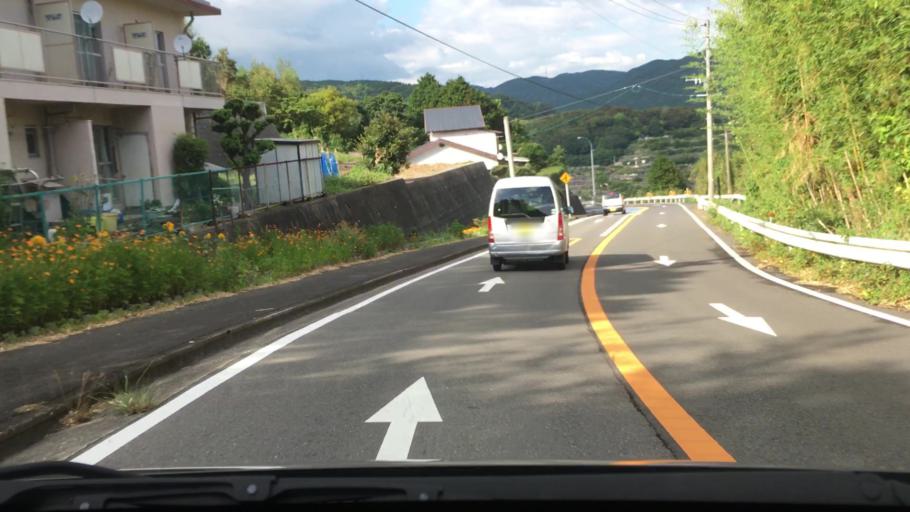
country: JP
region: Nagasaki
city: Togitsu
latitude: 32.8387
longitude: 129.7095
